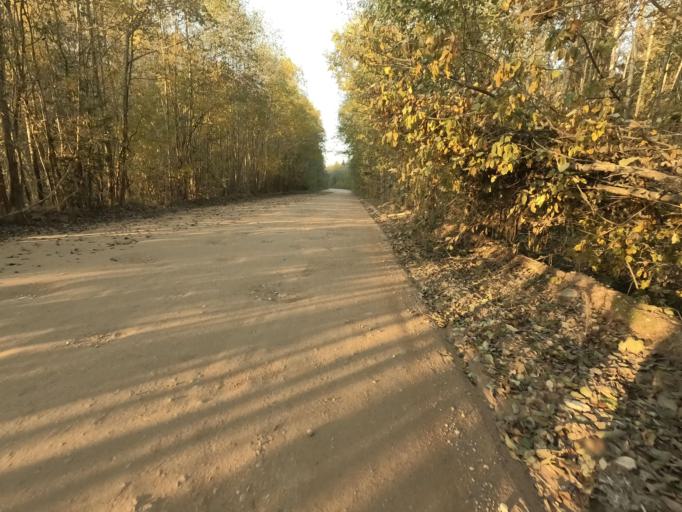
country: RU
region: Leningrad
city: Lyuban'
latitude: 58.9919
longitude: 31.1050
